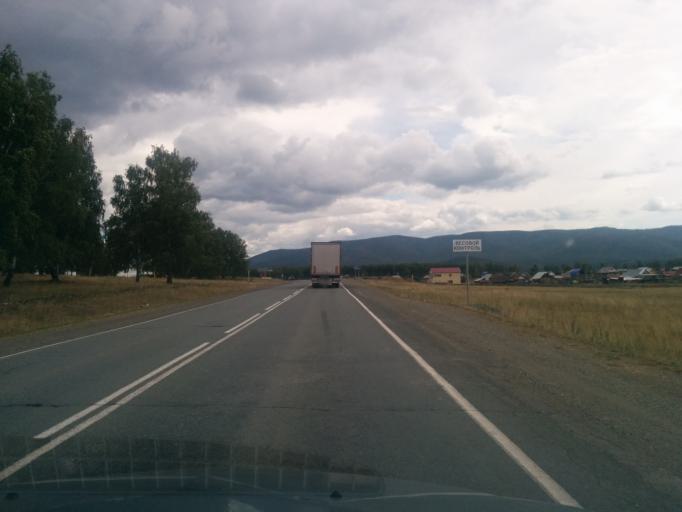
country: RU
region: Bashkortostan
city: Lomovka
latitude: 53.8854
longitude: 58.0989
